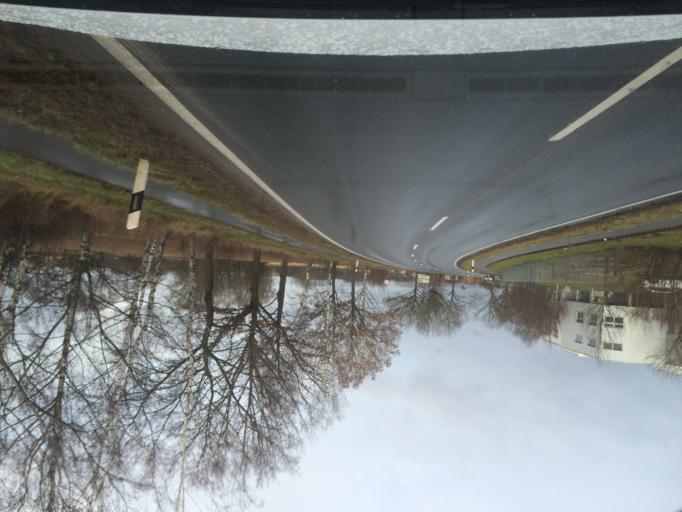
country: DE
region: Lower Saxony
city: Duderstadt
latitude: 51.5177
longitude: 10.2410
